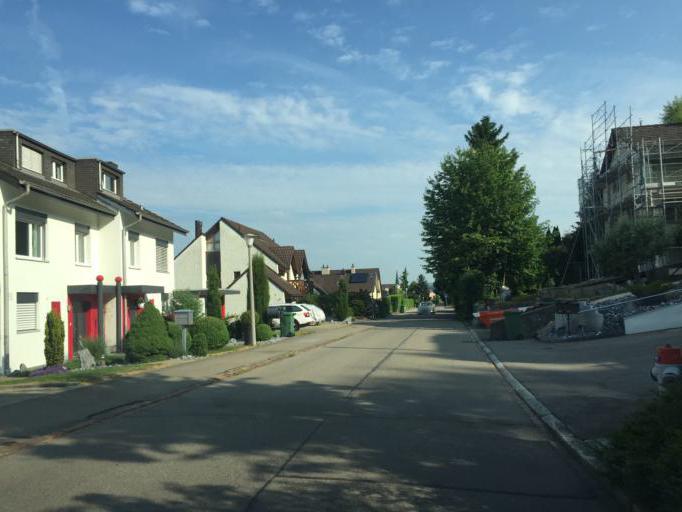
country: CH
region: Zurich
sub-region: Bezirk Buelach
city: Bachenbulach
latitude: 47.5071
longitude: 8.5476
